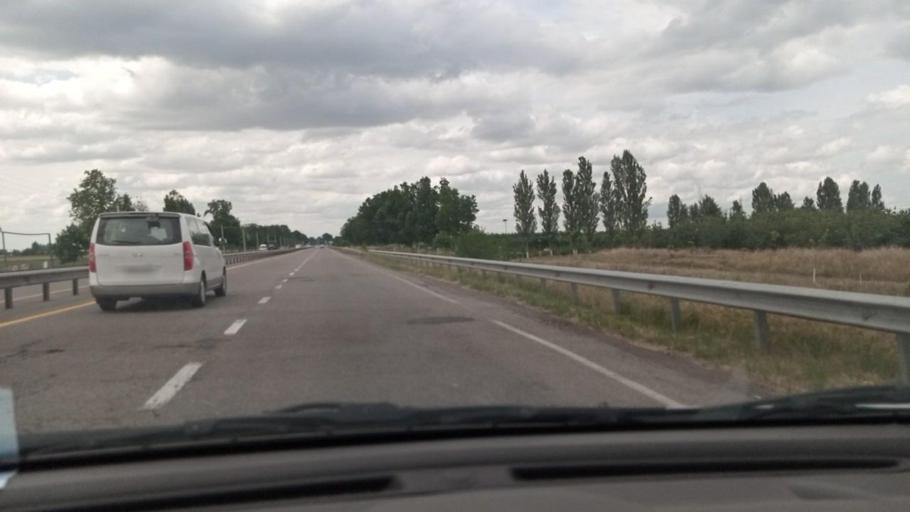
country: UZ
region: Toshkent Shahri
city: Bektemir
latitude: 41.1722
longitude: 69.4130
